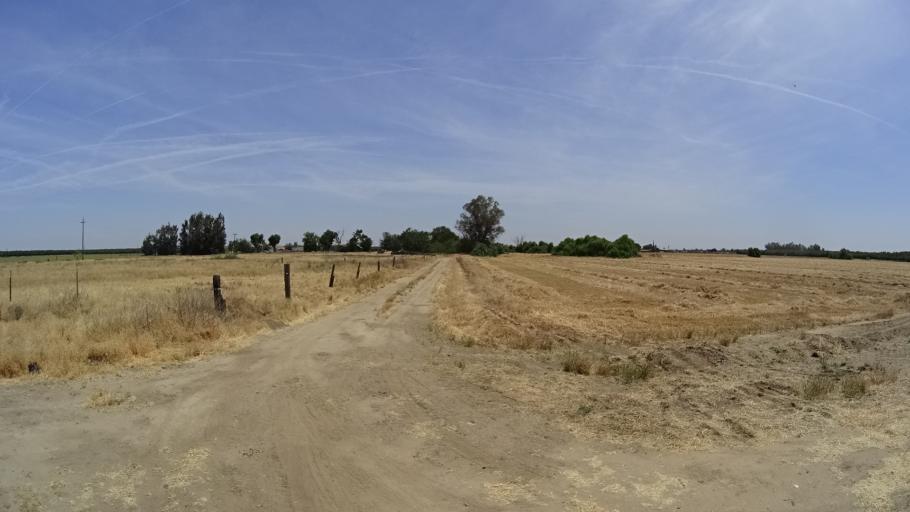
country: US
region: California
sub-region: Fresno County
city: Riverdale
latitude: 36.3937
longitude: -119.8783
